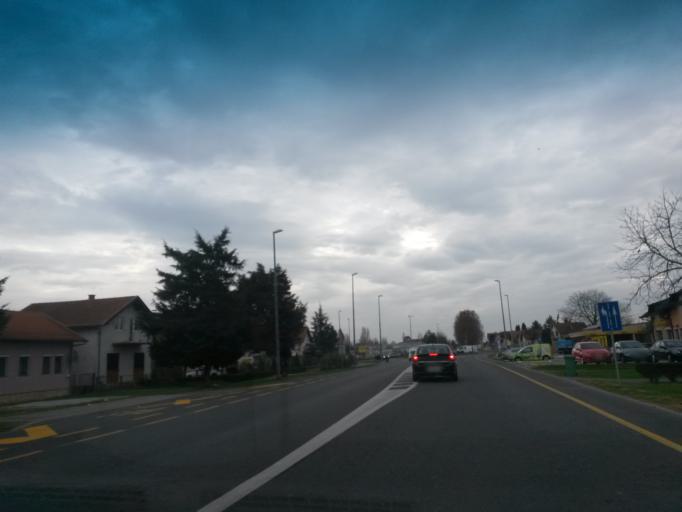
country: HR
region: Vukovarsko-Srijemska
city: Borovo
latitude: 45.3737
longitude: 18.9488
